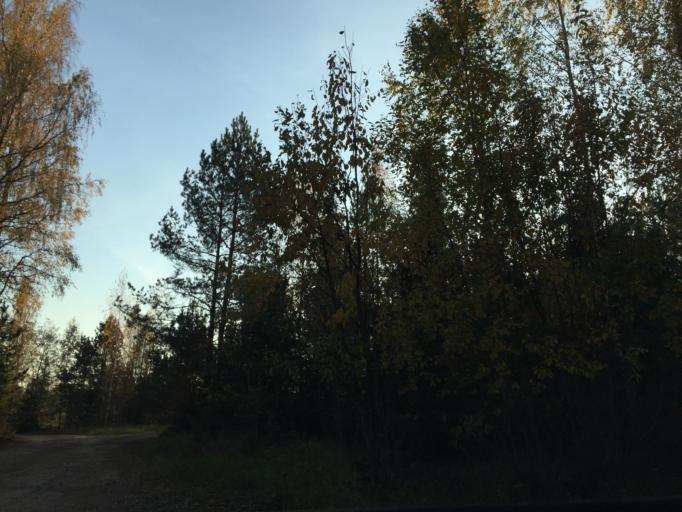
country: LV
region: Vainode
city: Vainode
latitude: 56.5876
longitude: 21.8321
